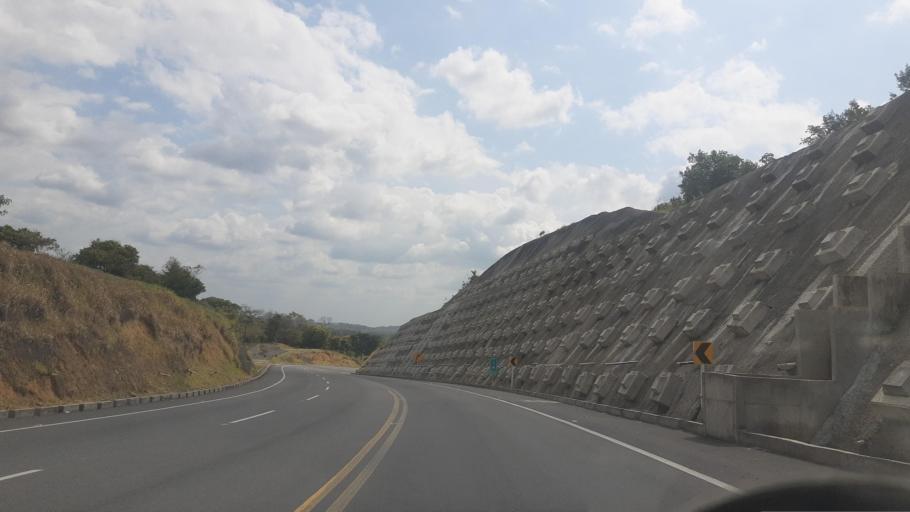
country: CO
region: Casanare
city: Monterrey
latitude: 4.8328
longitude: -72.8226
